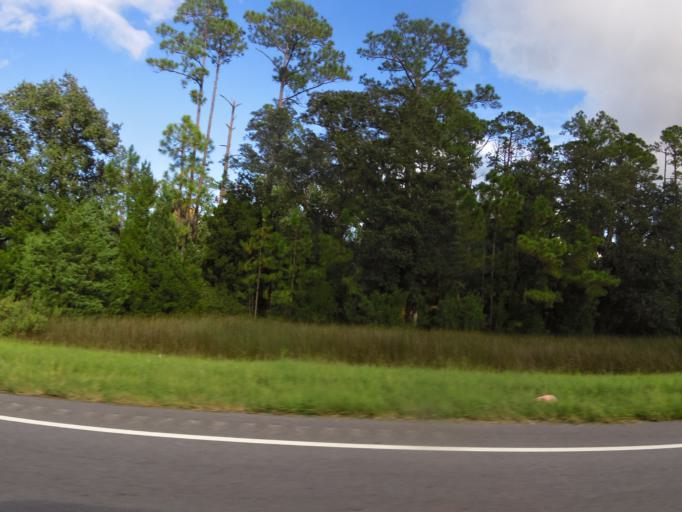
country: US
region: Georgia
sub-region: Glynn County
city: Country Club Estates
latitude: 31.1971
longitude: -81.4684
